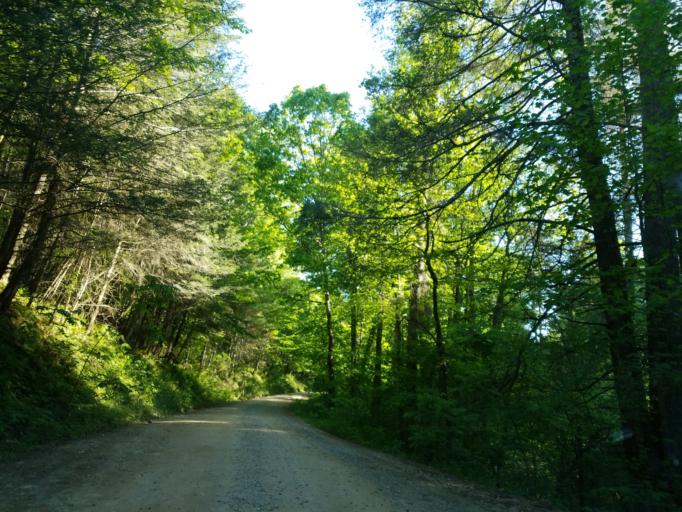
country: US
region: Georgia
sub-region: Fannin County
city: Blue Ridge
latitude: 34.7218
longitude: -84.1497
